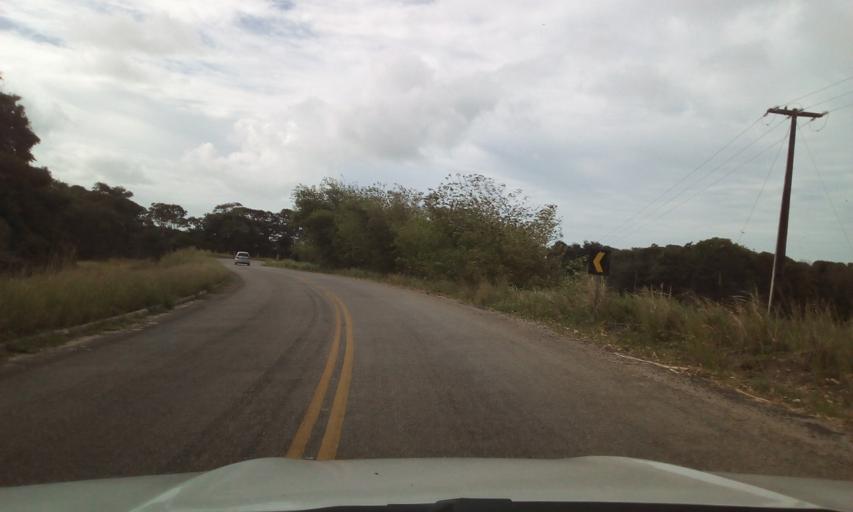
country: BR
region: Paraiba
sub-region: Cabedelo
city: Cabedelo
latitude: -6.9229
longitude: -34.8985
